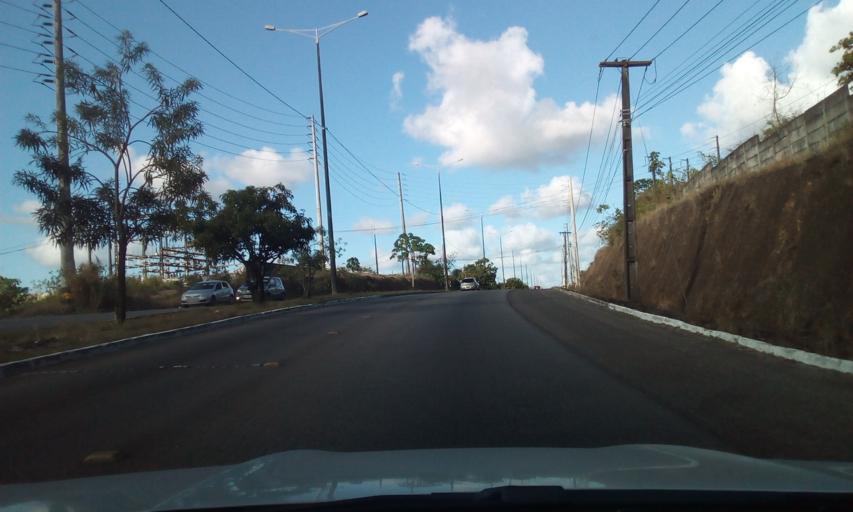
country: BR
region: Paraiba
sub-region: Bayeux
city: Bayeux
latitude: -7.1324
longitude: -34.9047
